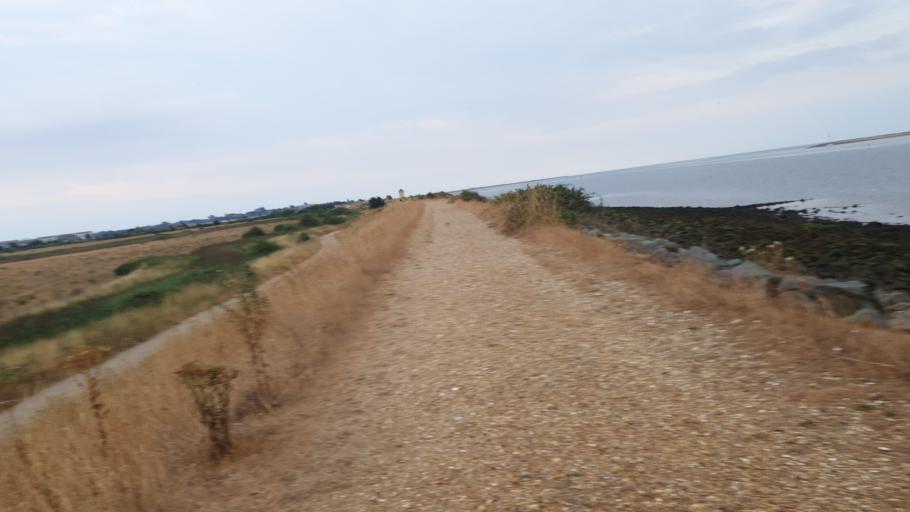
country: GB
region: England
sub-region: Essex
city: Brightlingsea
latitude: 51.8104
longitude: 1.0041
